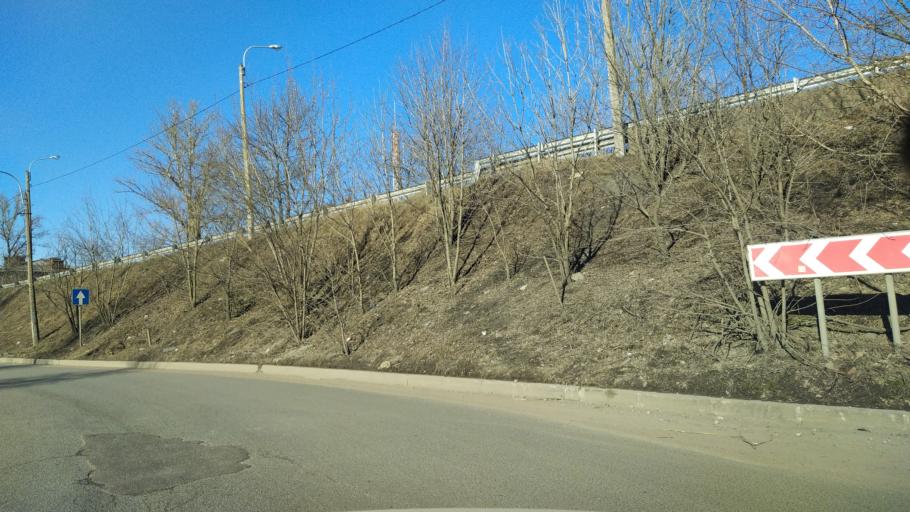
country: RU
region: St.-Petersburg
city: Centralniy
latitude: 59.9039
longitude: 30.3756
